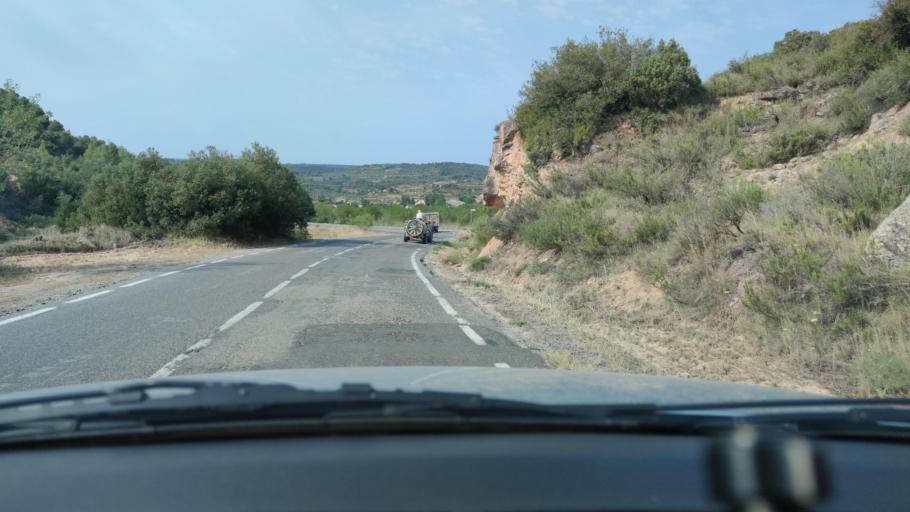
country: ES
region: Catalonia
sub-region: Provincia de Lleida
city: Juncosa
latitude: 41.4337
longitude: 0.8628
